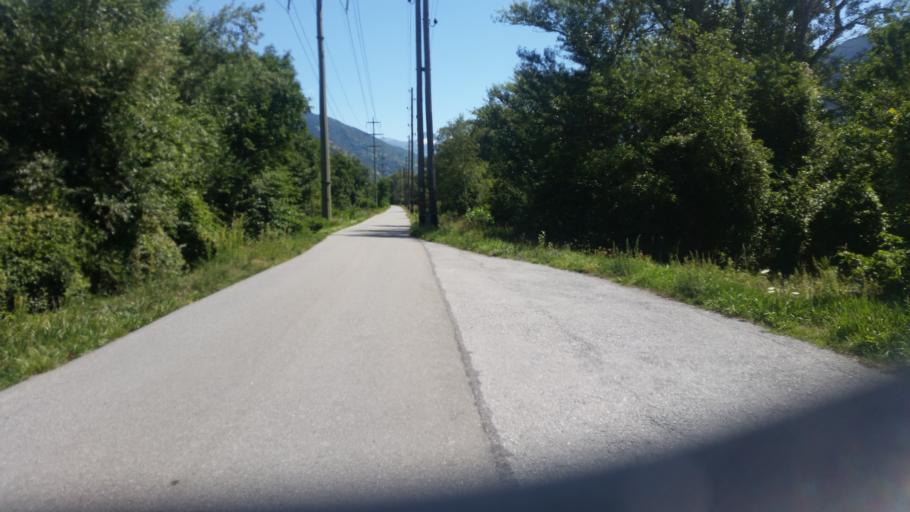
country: CH
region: Valais
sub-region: Raron District
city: Raron
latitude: 46.3072
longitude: 7.8063
